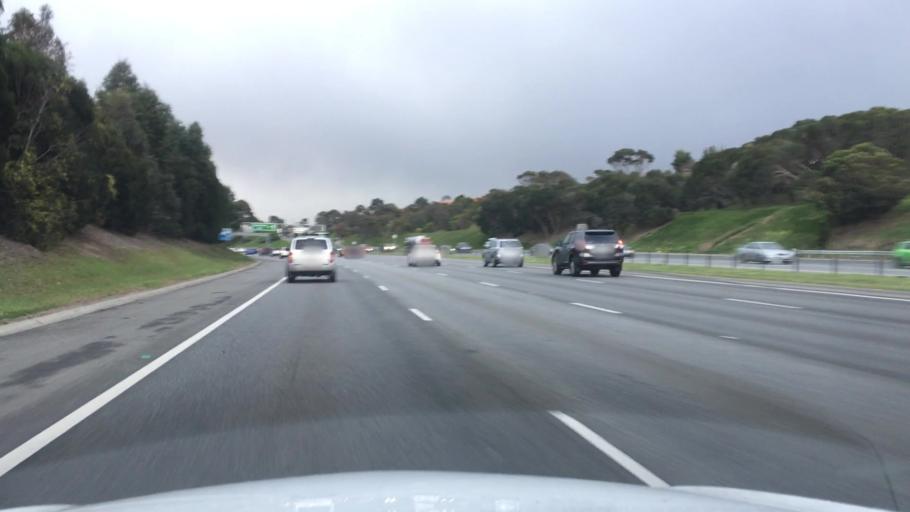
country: AU
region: Victoria
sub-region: Monash
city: Notting Hill
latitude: -37.8981
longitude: 145.1488
